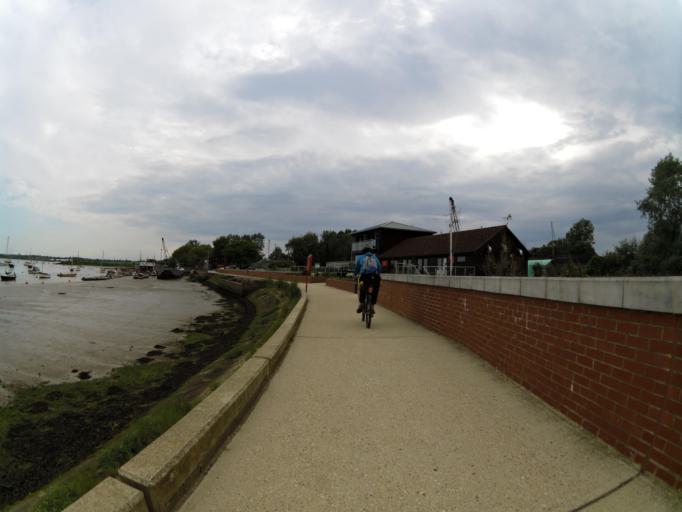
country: GB
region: England
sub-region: Suffolk
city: Woodbridge
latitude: 52.0892
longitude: 1.3173
